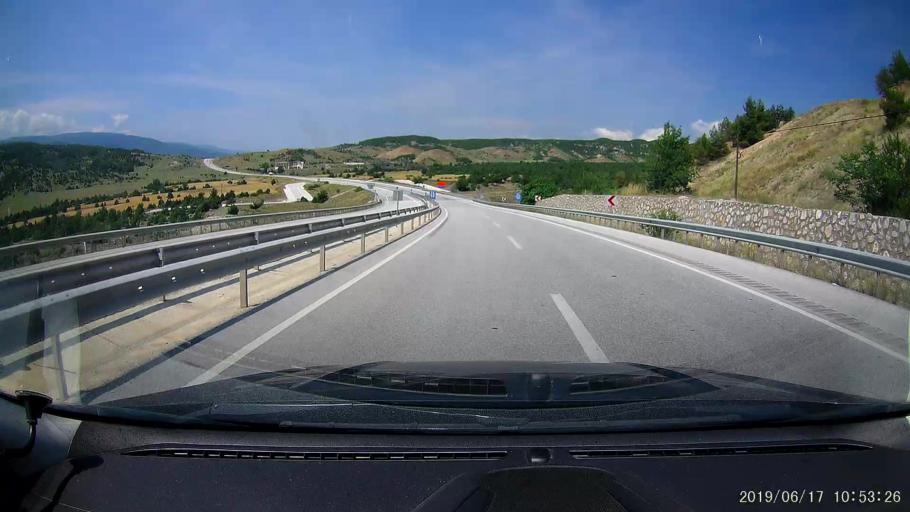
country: TR
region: Corum
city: Hacihamza
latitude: 41.0835
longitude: 34.3215
